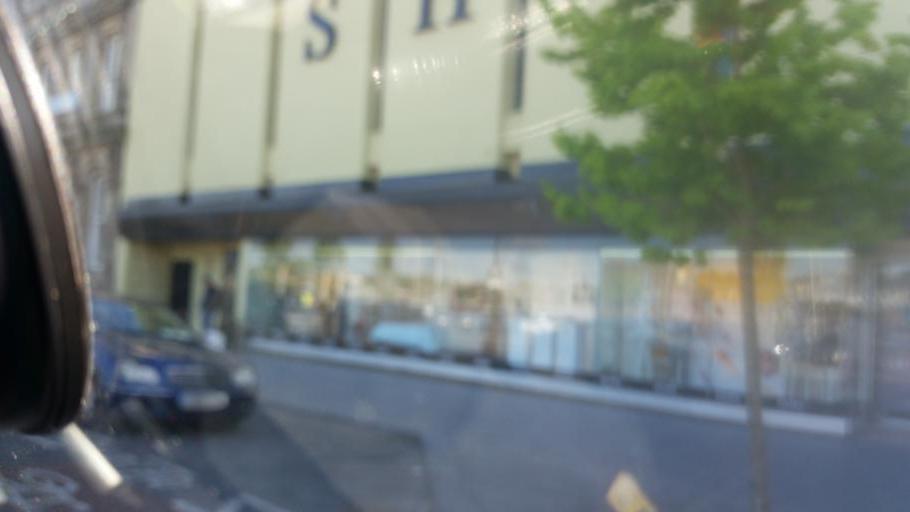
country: IE
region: Munster
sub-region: Waterford
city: Waterford
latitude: 52.2622
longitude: -7.1127
